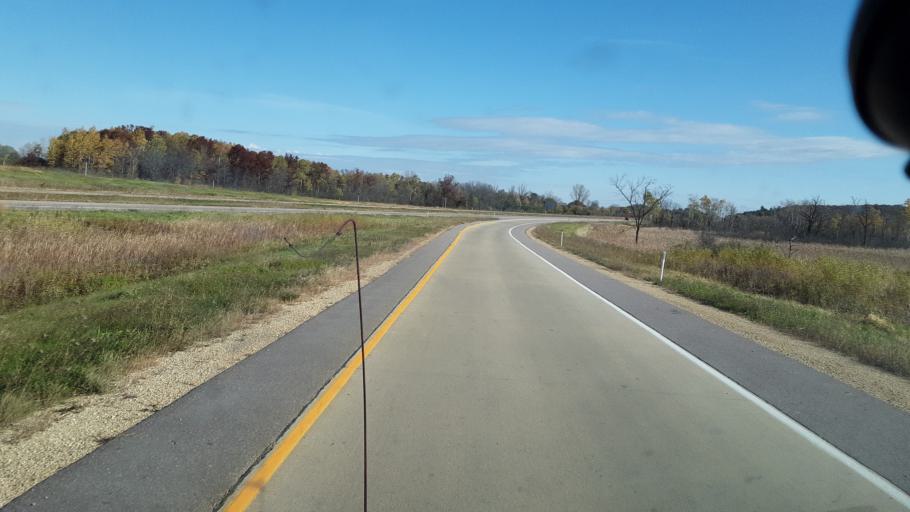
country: US
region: Wisconsin
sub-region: Monroe County
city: Tomah
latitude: 43.9574
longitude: -90.5031
